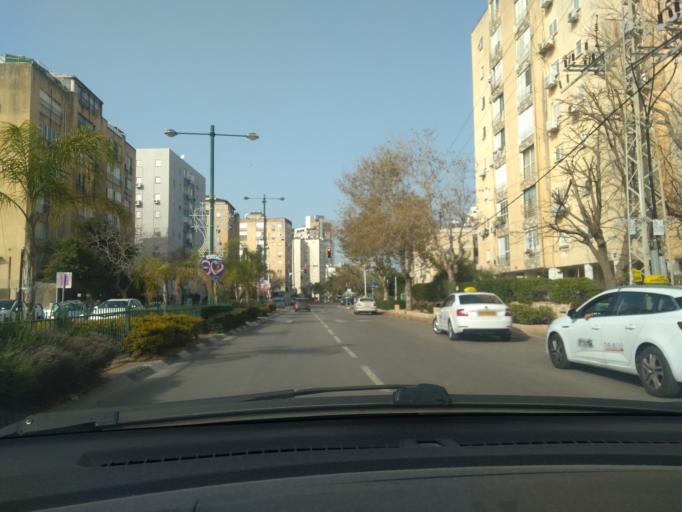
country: IL
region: Central District
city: Netanya
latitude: 32.3290
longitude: 34.8621
